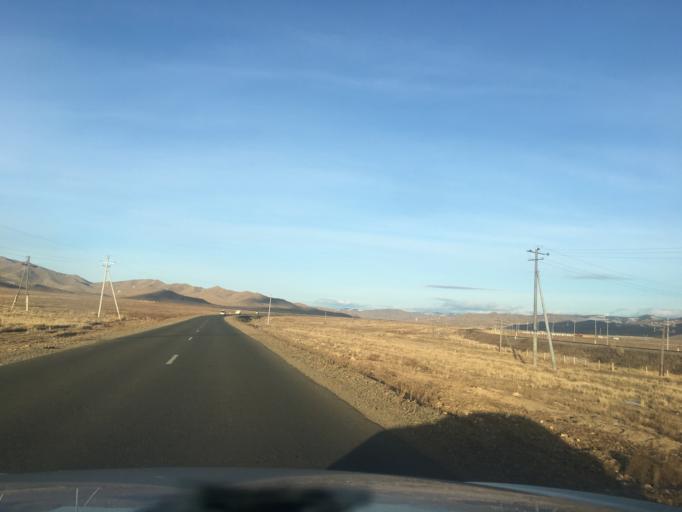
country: MN
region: Central Aimak
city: Ihsueuej
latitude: 48.0798
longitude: 106.5841
